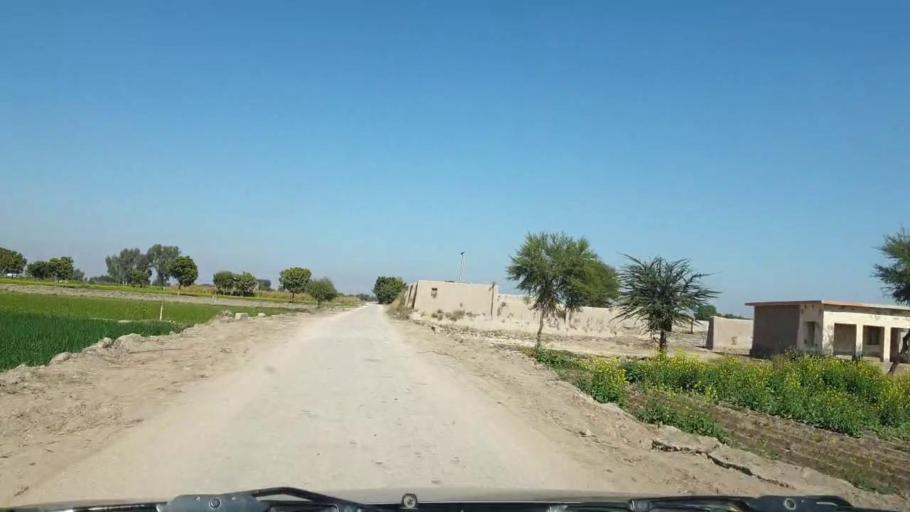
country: PK
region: Sindh
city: Khadro
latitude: 26.1409
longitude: 68.8158
